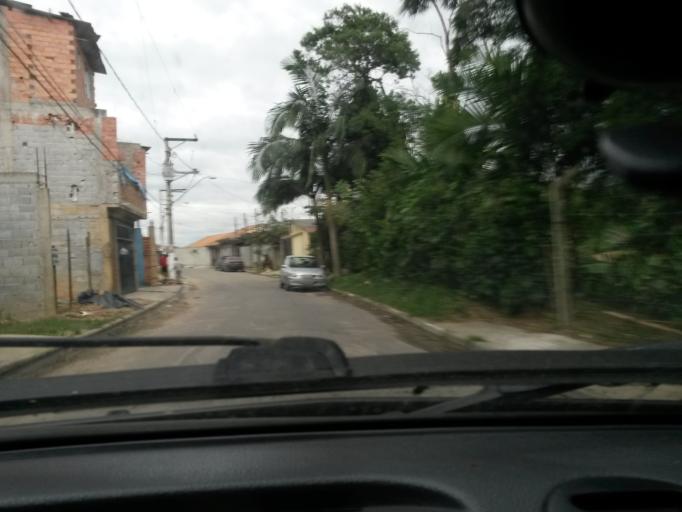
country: BR
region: Sao Paulo
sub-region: Sao Bernardo Do Campo
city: Sao Bernardo do Campo
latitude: -23.7995
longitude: -46.5368
